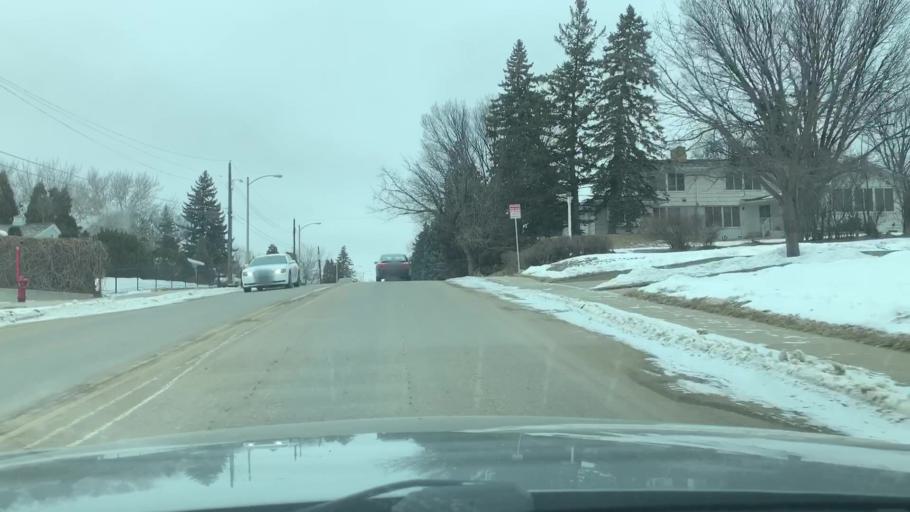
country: US
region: North Dakota
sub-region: Burleigh County
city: Bismarck
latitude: 46.8138
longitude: -100.7943
